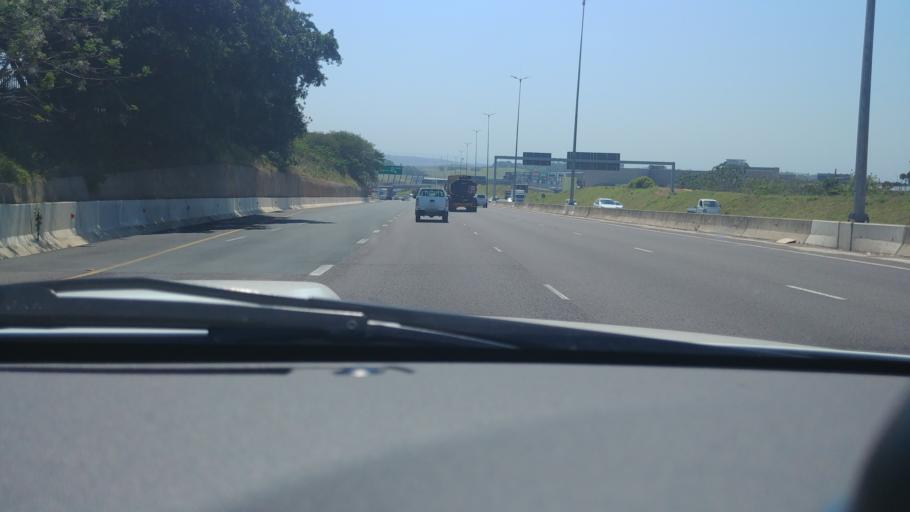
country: ZA
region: KwaZulu-Natal
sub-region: eThekwini Metropolitan Municipality
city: Durban
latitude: -29.7164
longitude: 31.0546
